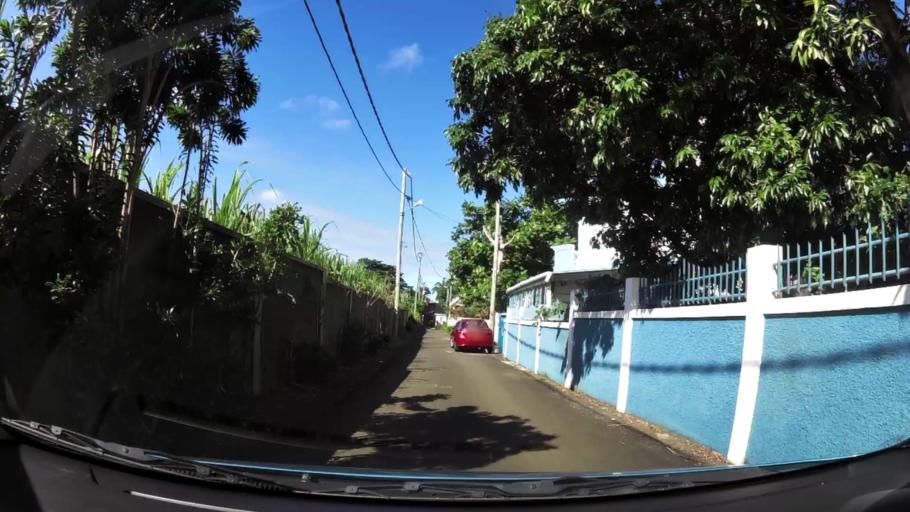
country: MU
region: Grand Port
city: Mahebourg
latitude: -20.4011
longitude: 57.6980
